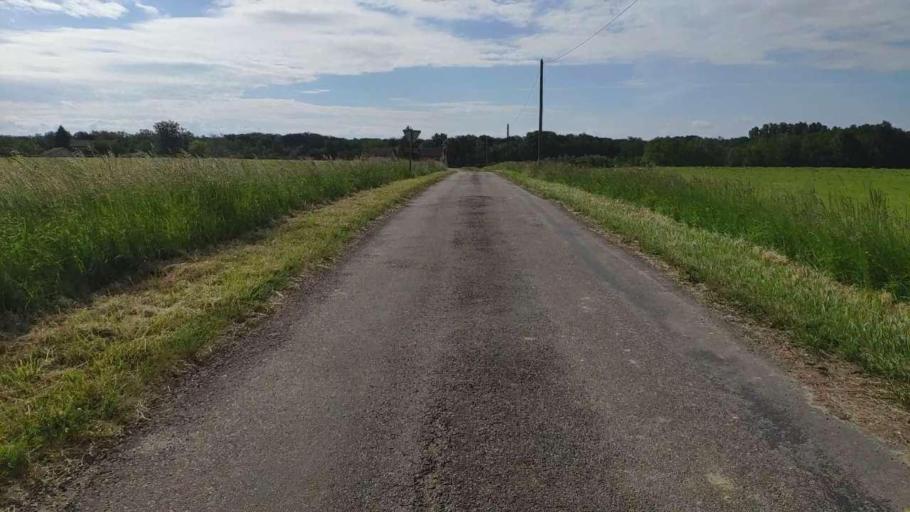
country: FR
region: Franche-Comte
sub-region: Departement du Jura
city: Bletterans
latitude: 46.7070
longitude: 5.4725
